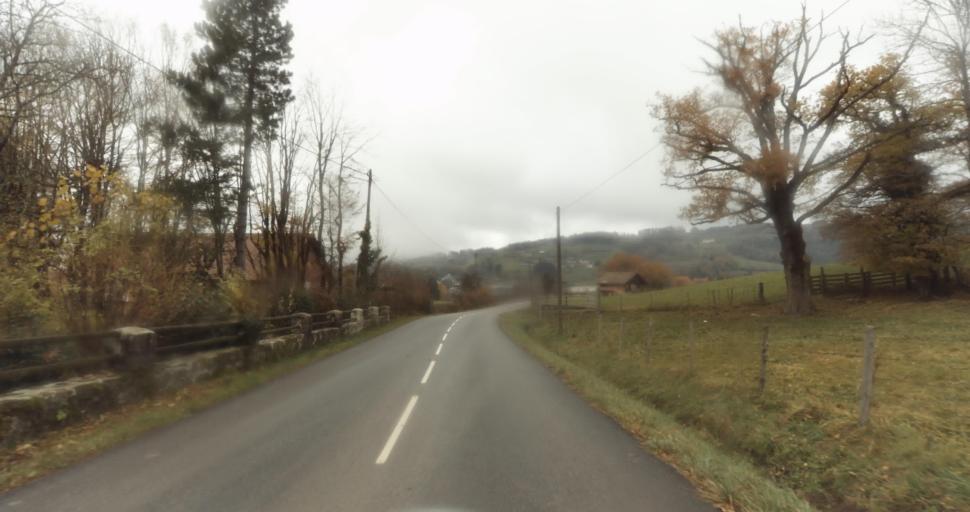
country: FR
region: Rhone-Alpes
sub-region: Departement de la Haute-Savoie
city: Thorens-Glieres
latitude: 45.9944
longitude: 6.2599
